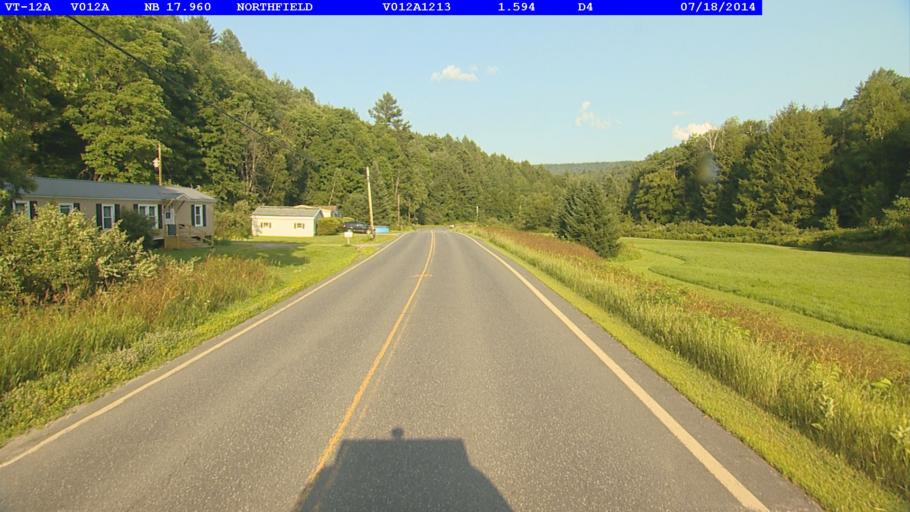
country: US
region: Vermont
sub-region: Washington County
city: Northfield
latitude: 44.1131
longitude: -72.6976
